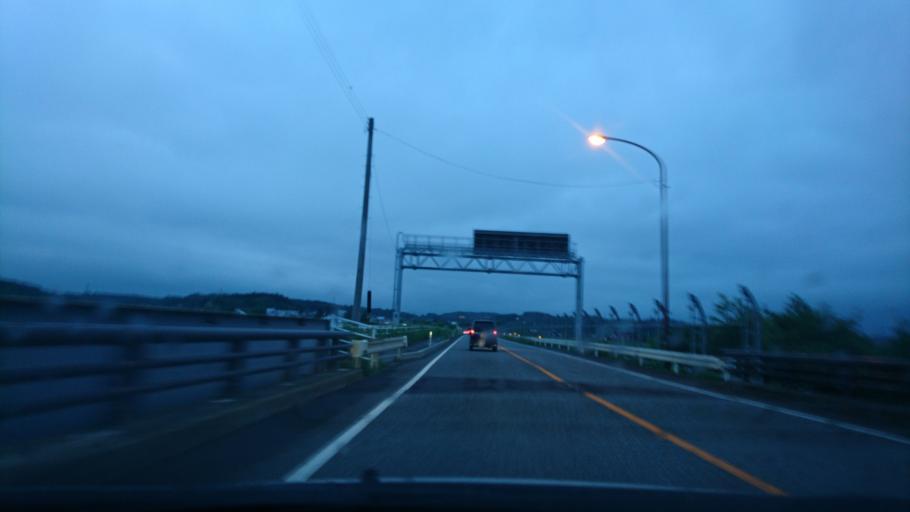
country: JP
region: Iwate
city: Ichinoseki
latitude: 38.8018
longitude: 141.0603
